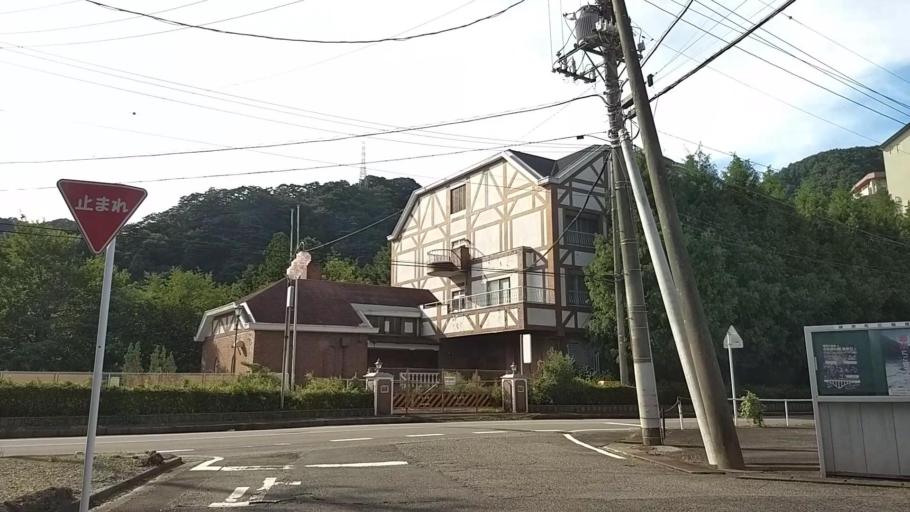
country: JP
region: Tochigi
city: Imaichi
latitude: 36.8188
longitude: 139.7102
